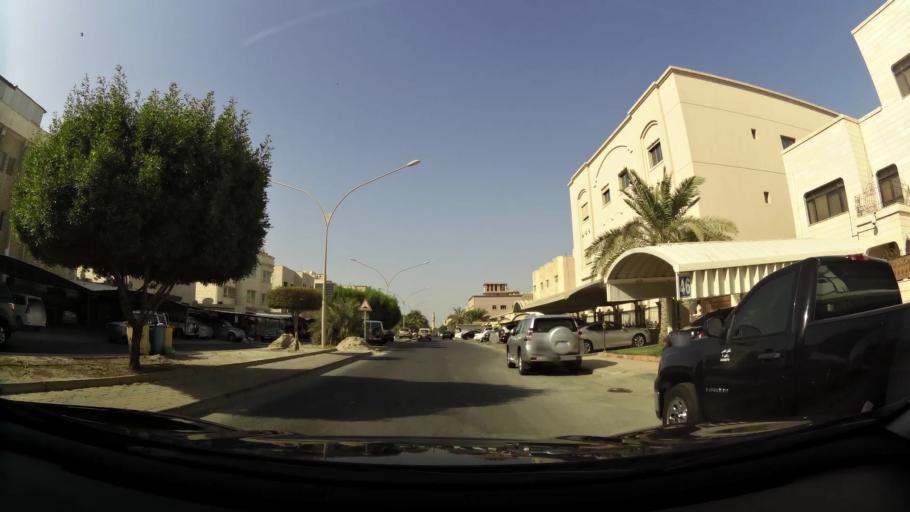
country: KW
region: Muhafazat Hawalli
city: Salwa
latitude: 29.2907
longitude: 48.0782
